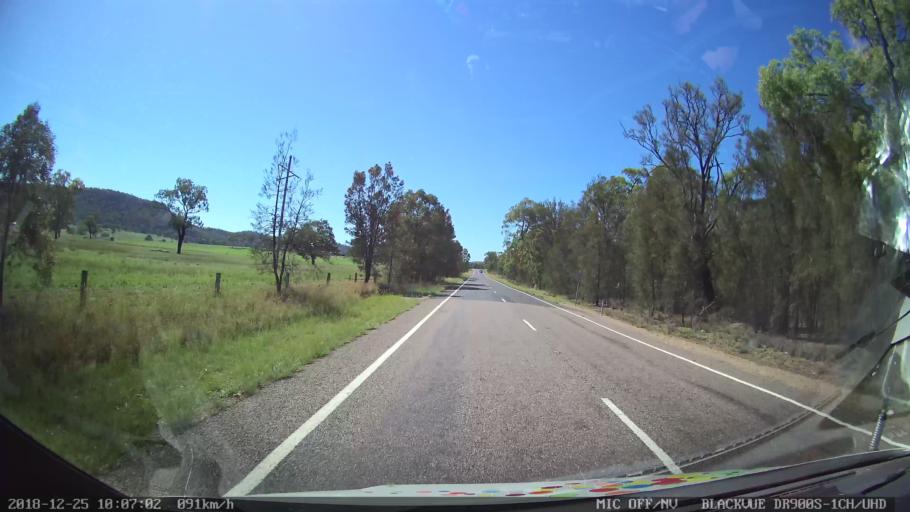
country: AU
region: New South Wales
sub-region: Upper Hunter Shire
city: Merriwa
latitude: -32.2666
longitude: 150.4948
